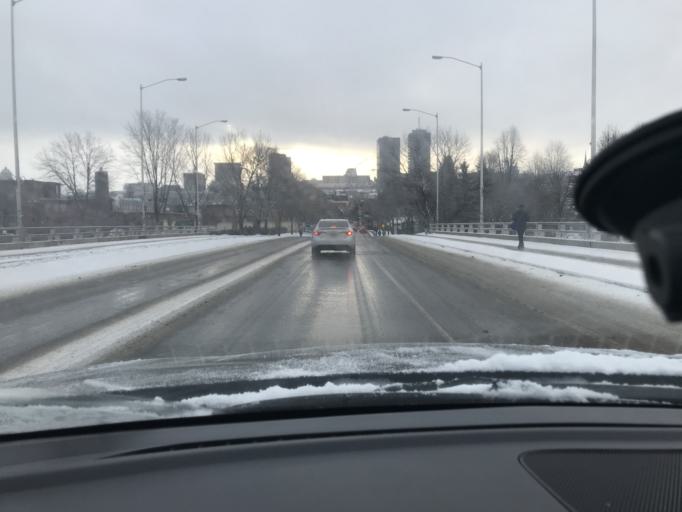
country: CA
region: Quebec
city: Quebec
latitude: 46.8194
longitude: -71.2238
